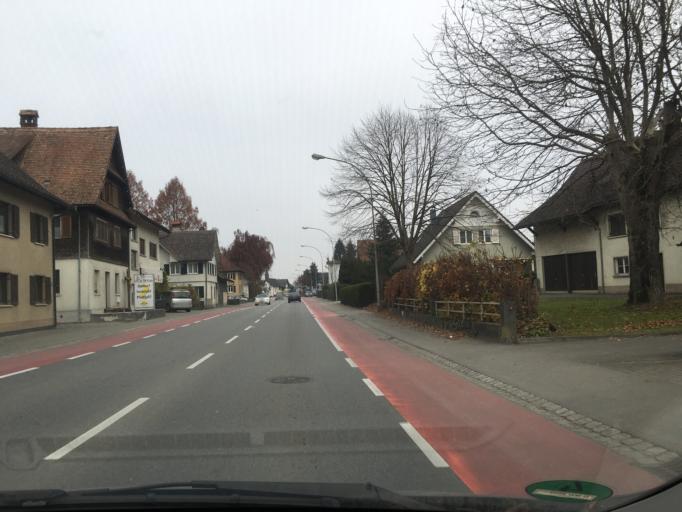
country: AT
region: Vorarlberg
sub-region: Politischer Bezirk Feldkirch
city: Altach
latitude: 47.3573
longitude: 9.6637
